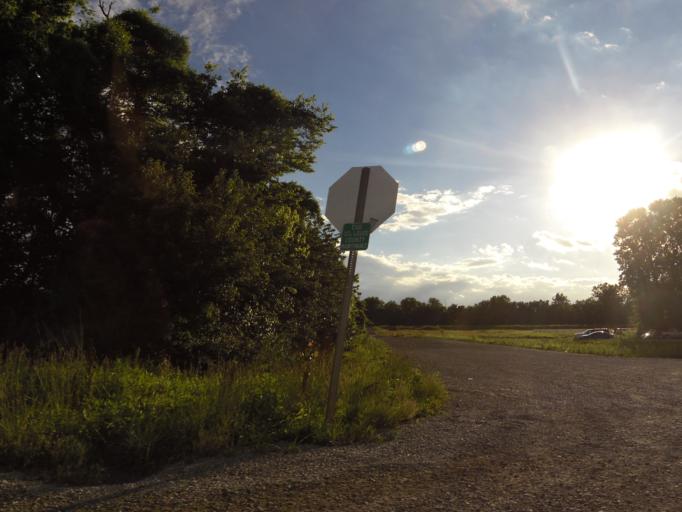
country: US
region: Missouri
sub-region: Saint Charles County
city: Weldon Spring
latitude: 38.6645
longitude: -90.6752
